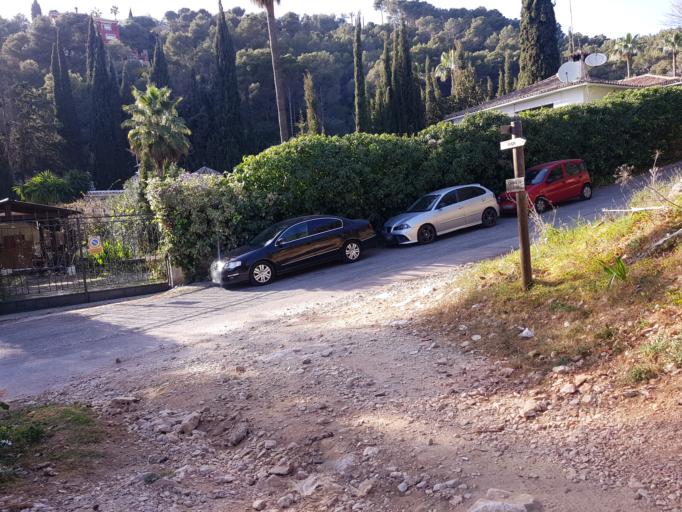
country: ES
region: Andalusia
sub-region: Provincia de Malaga
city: Marbella
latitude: 36.5301
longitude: -4.8849
